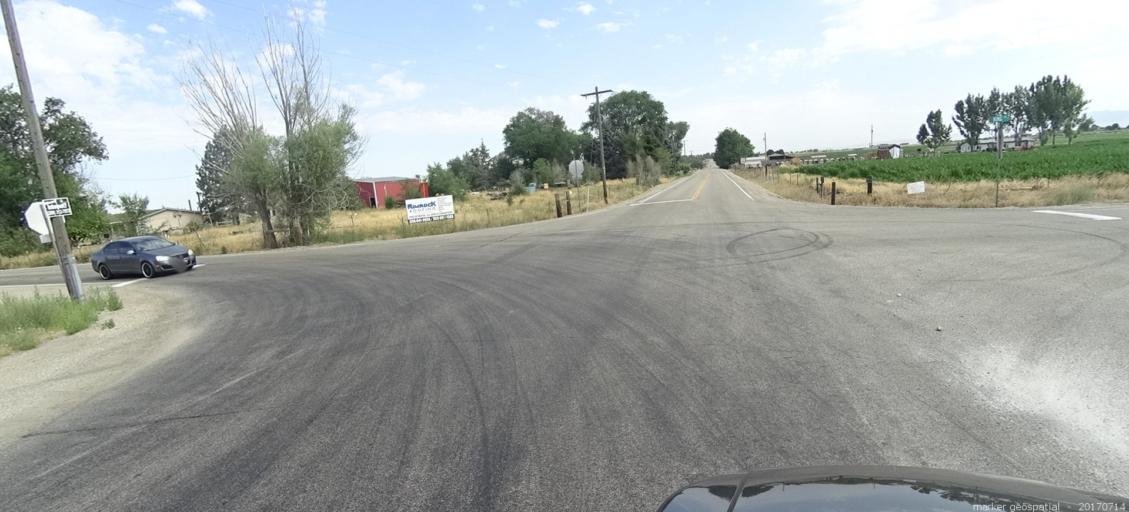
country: US
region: Idaho
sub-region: Ada County
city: Kuna
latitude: 43.4735
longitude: -116.3545
